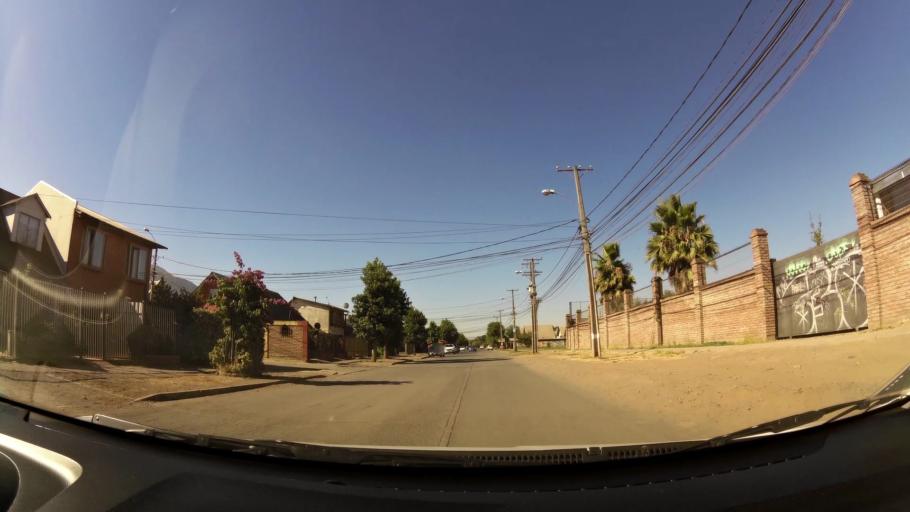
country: CL
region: O'Higgins
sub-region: Provincia de Colchagua
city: Chimbarongo
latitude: -34.5798
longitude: -71.0009
